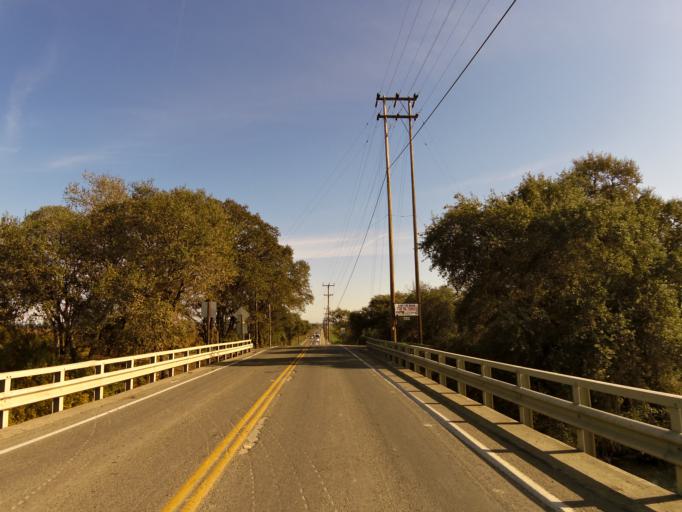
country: US
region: California
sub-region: Sacramento County
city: Walnut Grove
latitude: 38.2768
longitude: -121.4960
